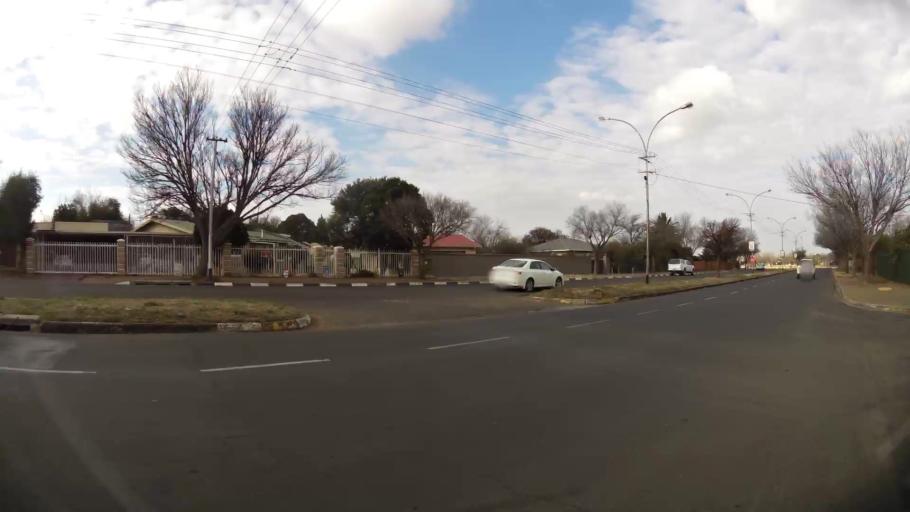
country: ZA
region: Orange Free State
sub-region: Mangaung Metropolitan Municipality
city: Bloemfontein
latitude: -29.0810
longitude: 26.2119
